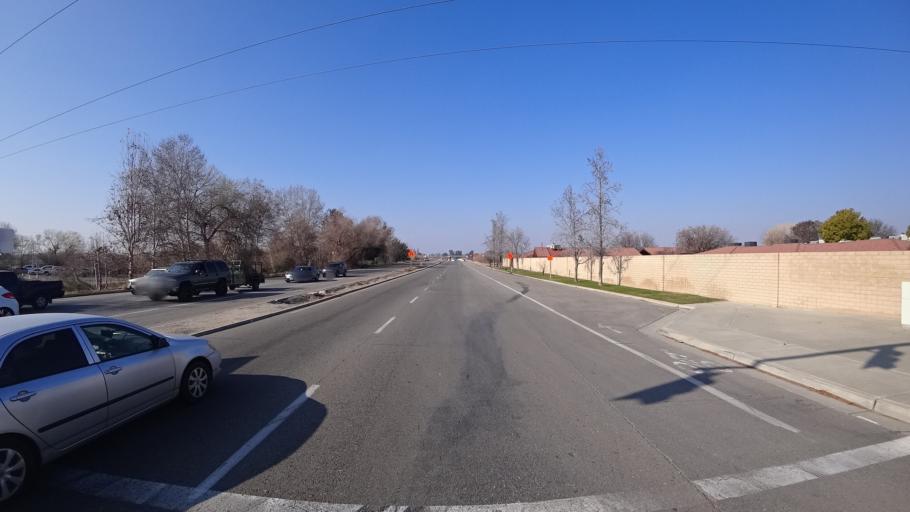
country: US
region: California
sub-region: Kern County
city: Oildale
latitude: 35.4047
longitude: -119.0071
